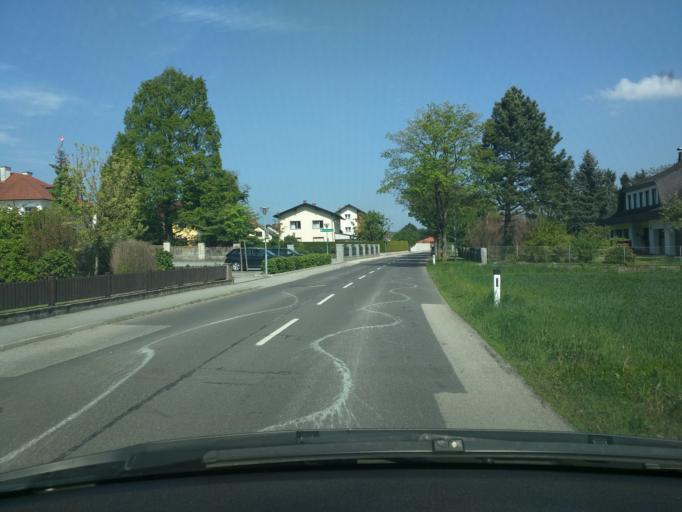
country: AT
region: Lower Austria
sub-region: Politischer Bezirk Amstetten
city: Sankt Georgen am Ybbsfelde
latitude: 48.1295
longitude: 14.9560
